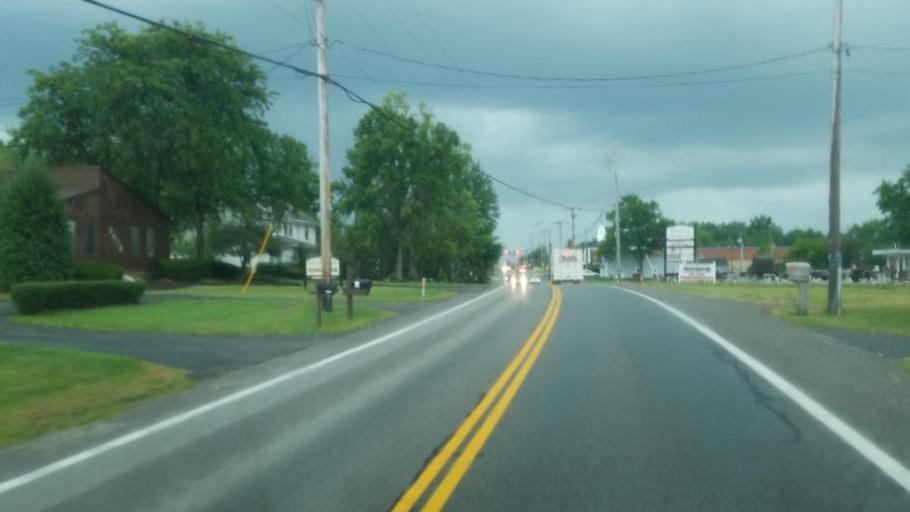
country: US
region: Ohio
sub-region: Trumbull County
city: Champion Heights
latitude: 41.2939
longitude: -80.8484
